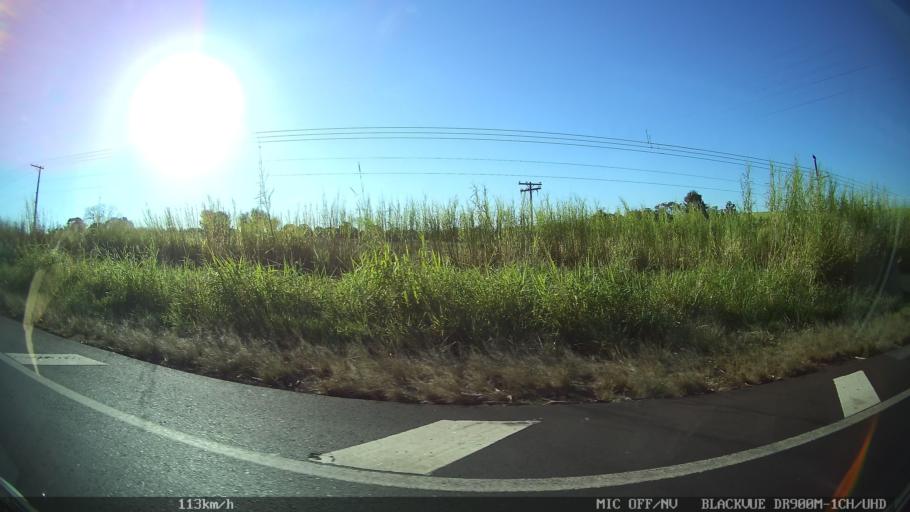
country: BR
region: Sao Paulo
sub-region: Olimpia
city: Olimpia
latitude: -20.7304
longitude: -49.0550
